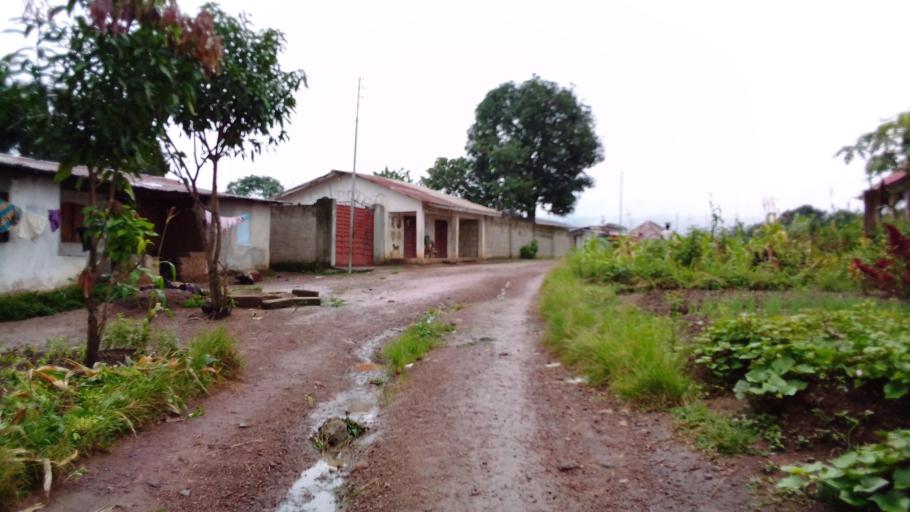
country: SL
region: Eastern Province
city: Kenema
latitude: 7.8696
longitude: -11.1736
